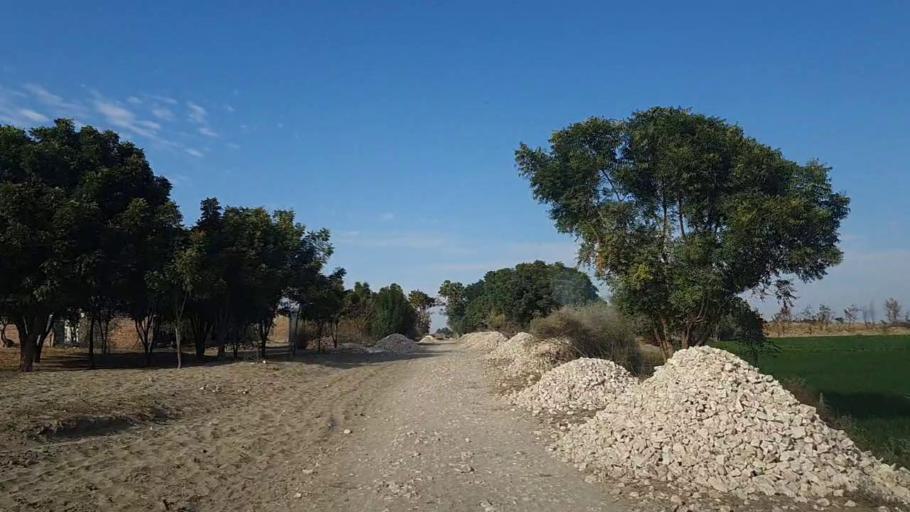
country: PK
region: Sindh
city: Jam Sahib
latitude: 26.3097
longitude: 68.8141
